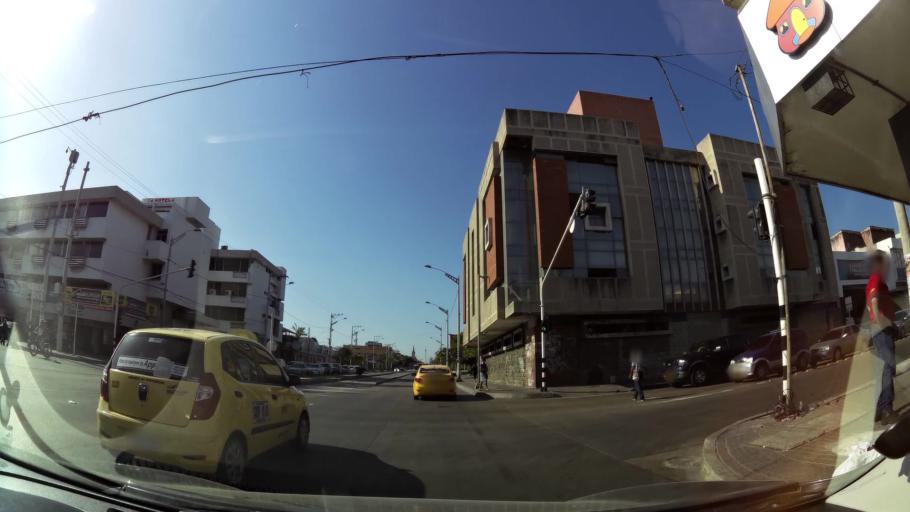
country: CO
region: Atlantico
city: Barranquilla
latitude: 10.9799
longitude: -74.7872
